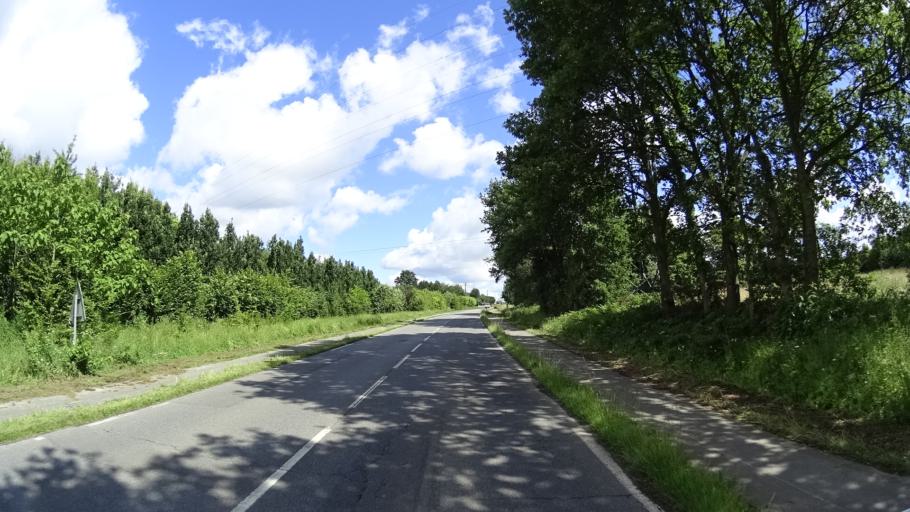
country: FR
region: Brittany
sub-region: Departement d'Ille-et-Vilaine
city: Le Rheu
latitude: 48.1144
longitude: -1.8069
